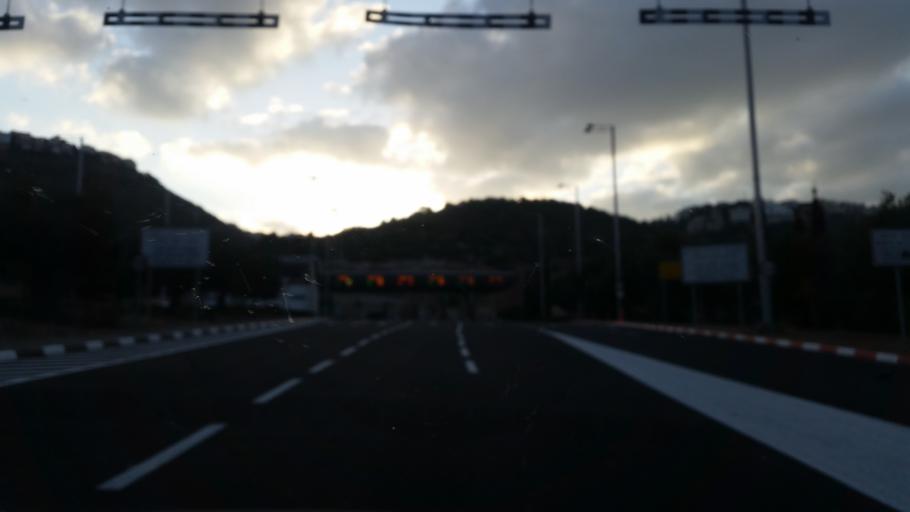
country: IL
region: Haifa
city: Tirat Karmel
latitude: 32.7924
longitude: 34.9680
